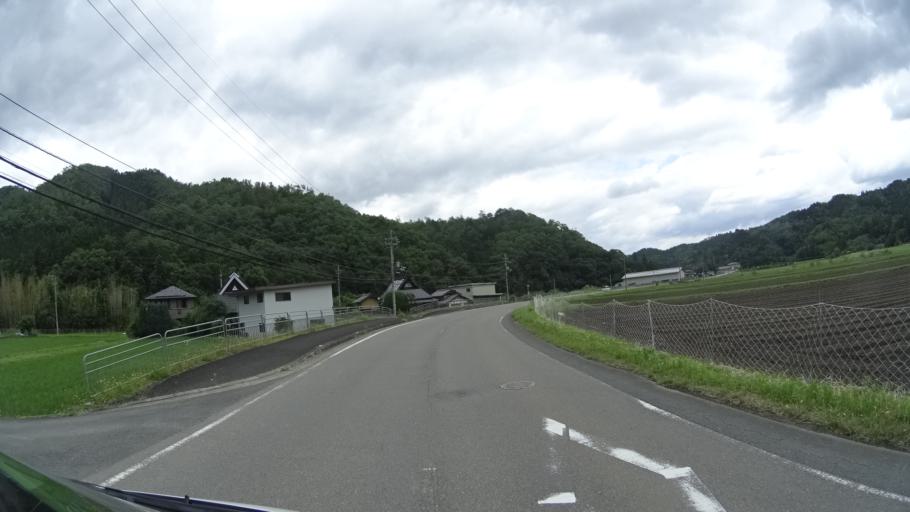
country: JP
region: Kyoto
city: Kameoka
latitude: 35.0951
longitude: 135.4279
